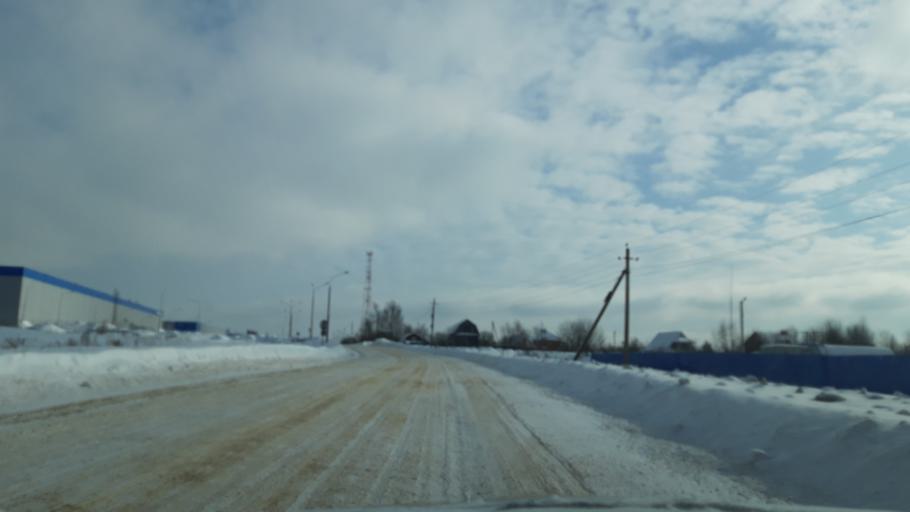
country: RU
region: Moskovskaya
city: Yermolino
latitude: 56.1453
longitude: 37.3727
